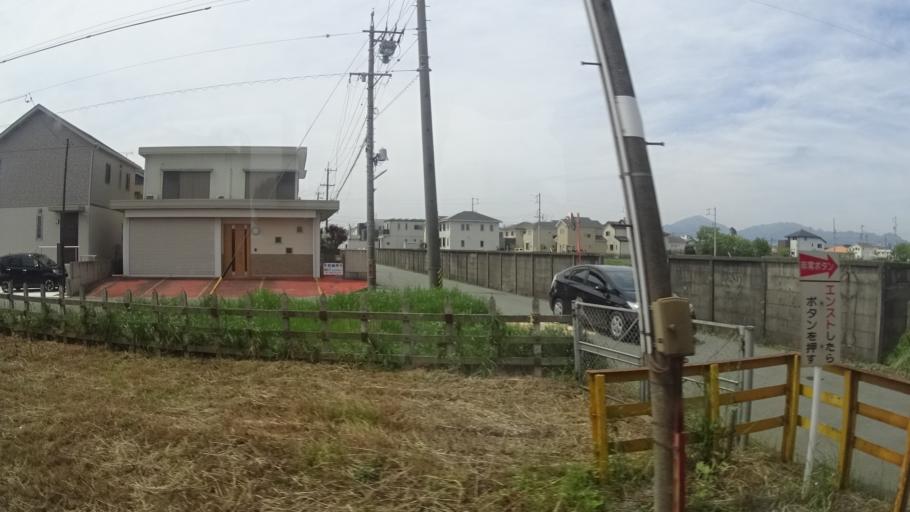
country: JP
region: Mie
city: Hisai-motomachi
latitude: 34.5674
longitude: 136.5442
